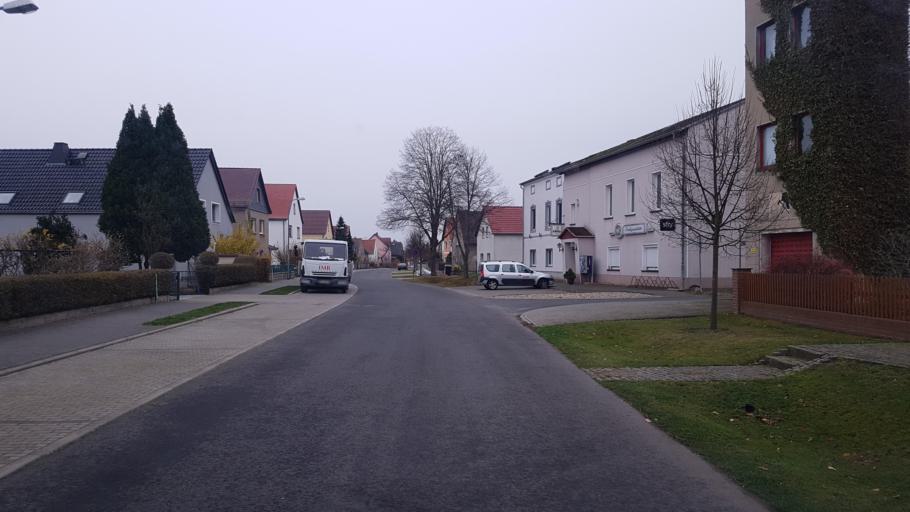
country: DE
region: Brandenburg
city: Lindenau
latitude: 51.3998
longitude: 13.7190
